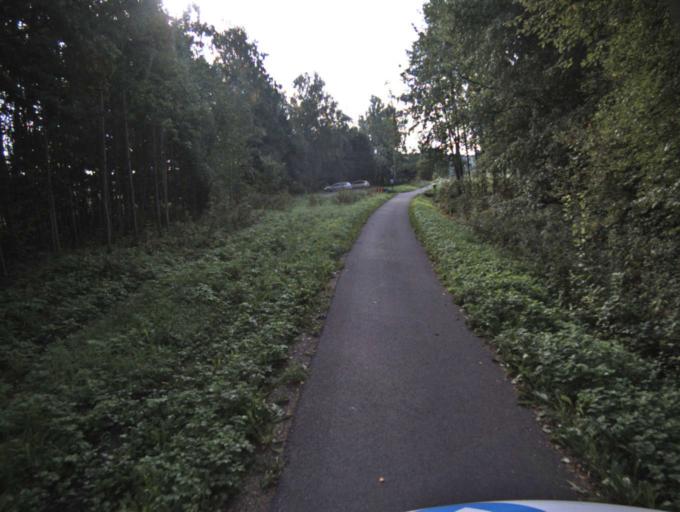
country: SE
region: Vaestra Goetaland
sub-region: Ulricehamns Kommun
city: Ulricehamn
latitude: 57.7420
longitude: 13.3982
